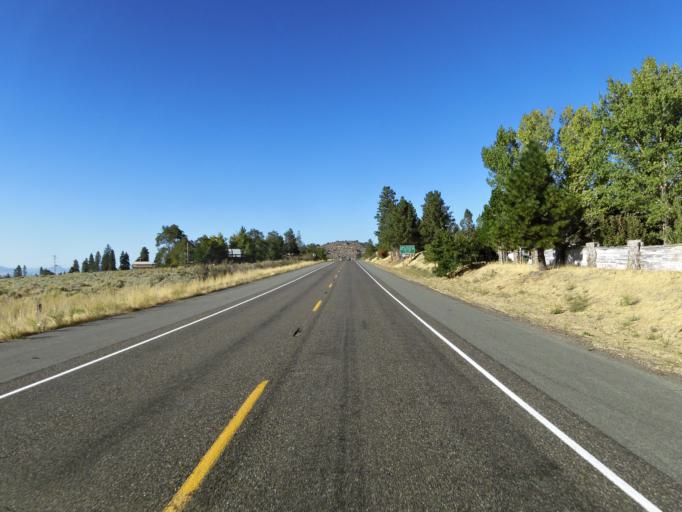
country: US
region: California
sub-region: Siskiyou County
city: Weed
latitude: 41.4679
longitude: -122.3534
